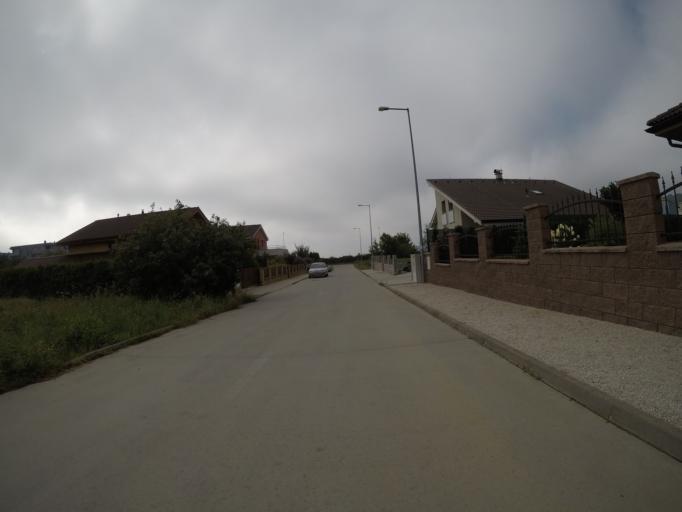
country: SK
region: Trenciansky
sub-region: Okres Nove Mesto nad Vahom
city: Nove Mesto nad Vahom
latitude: 48.7570
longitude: 17.8150
